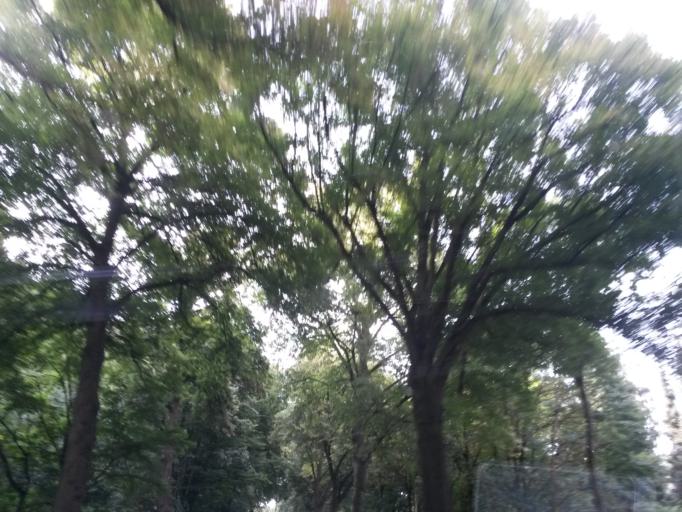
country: DE
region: North Rhine-Westphalia
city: Lohmar
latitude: 50.8663
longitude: 7.2069
